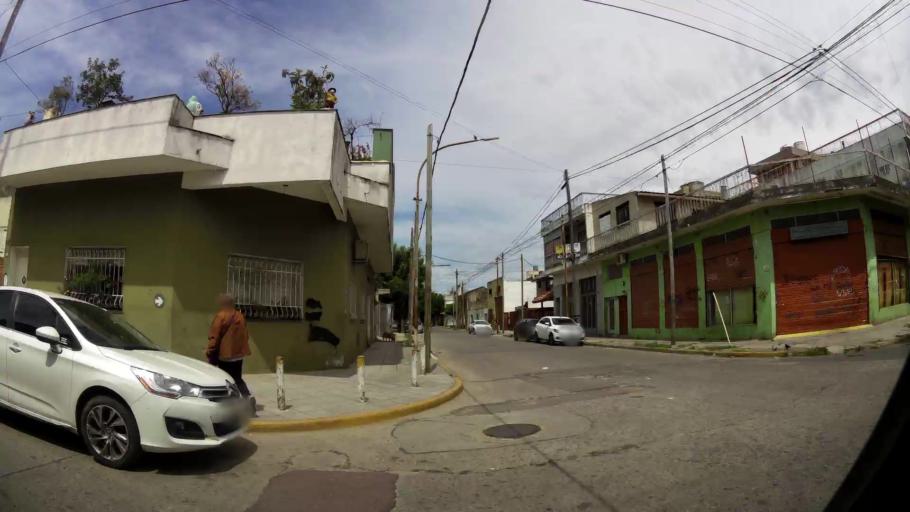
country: AR
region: Buenos Aires
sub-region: Partido de Lanus
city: Lanus
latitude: -34.6676
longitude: -58.4109
